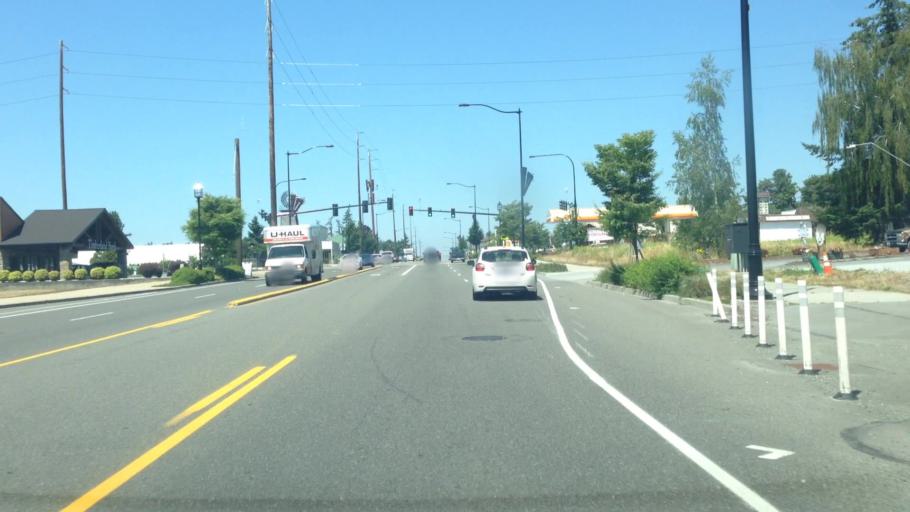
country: US
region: Washington
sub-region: Pierce County
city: Edgewood
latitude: 47.2344
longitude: -122.2939
